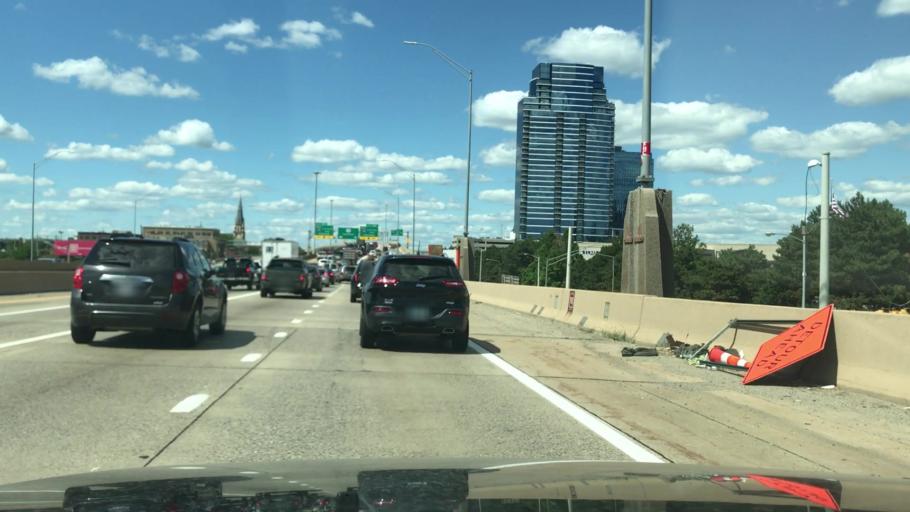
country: US
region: Michigan
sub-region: Kent County
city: Grand Rapids
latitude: 42.9663
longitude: -85.6785
